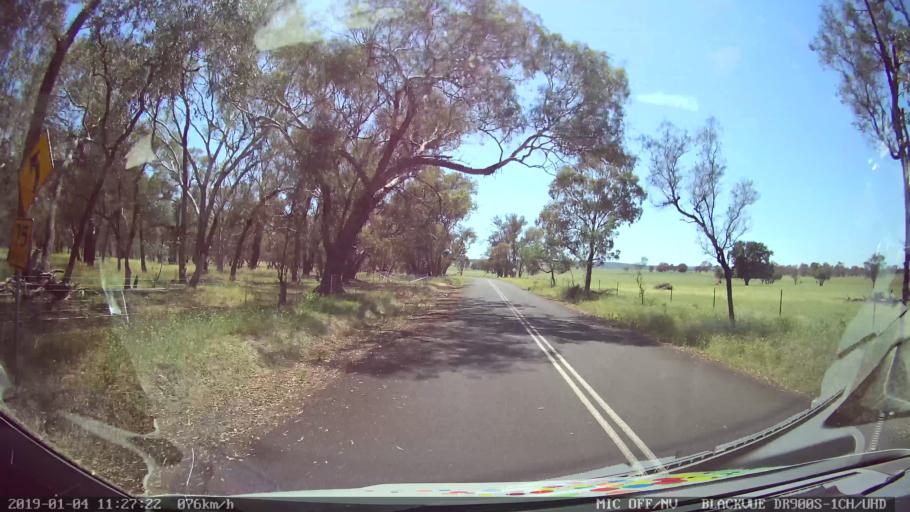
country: AU
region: New South Wales
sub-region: Cabonne
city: Molong
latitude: -33.1093
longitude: 148.7619
